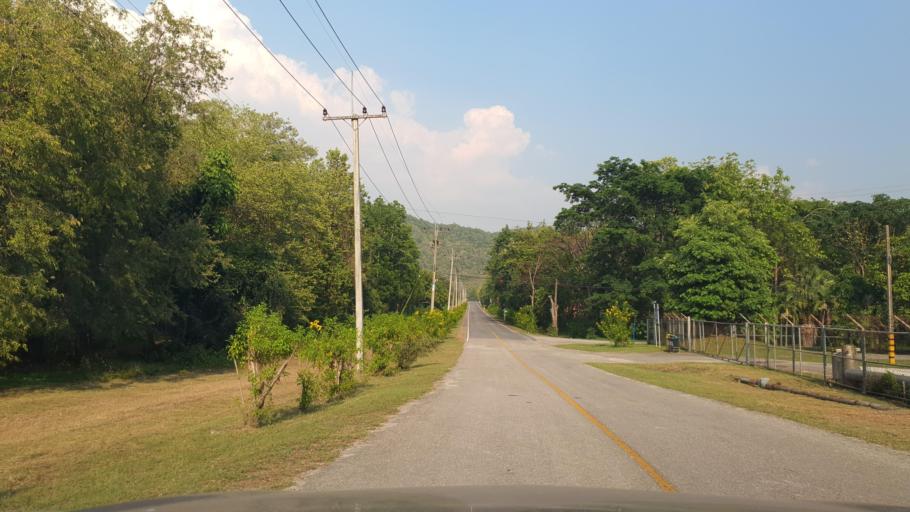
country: TH
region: Kanchanaburi
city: Sai Yok
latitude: 14.2300
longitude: 99.2304
